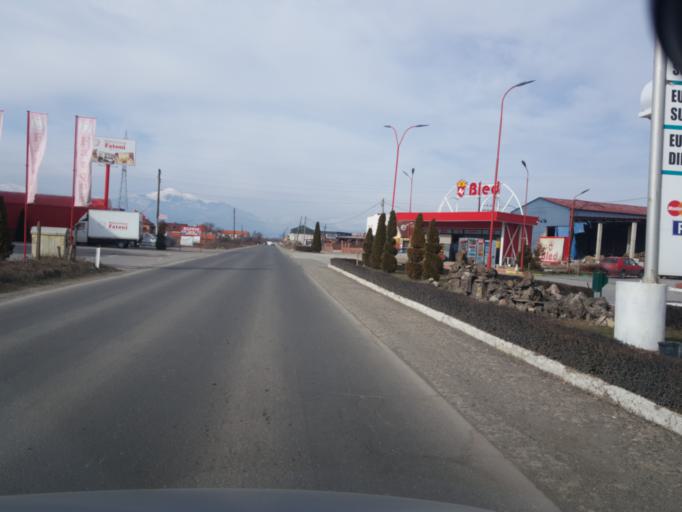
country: XK
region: Gjakova
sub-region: Komuna e Gjakoves
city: Gjakove
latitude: 42.4022
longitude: 20.4382
